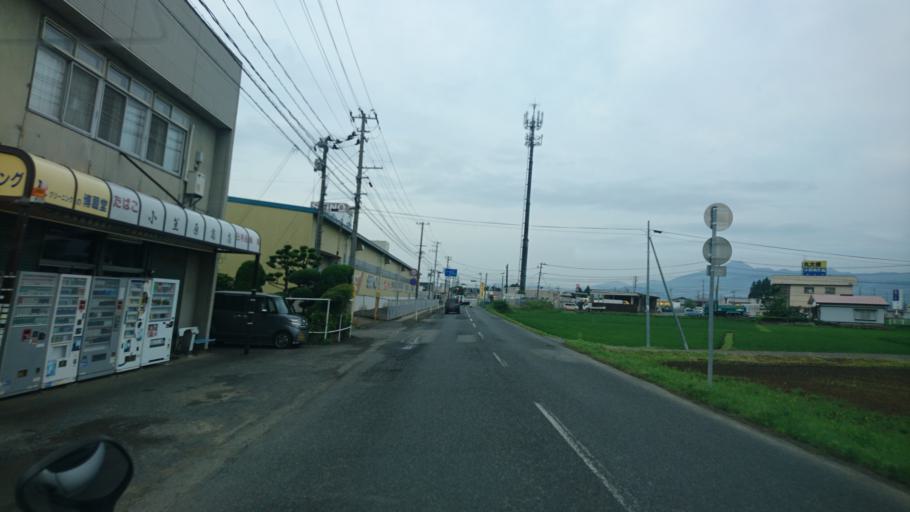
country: JP
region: Iwate
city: Morioka-shi
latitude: 39.6592
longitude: 141.1414
